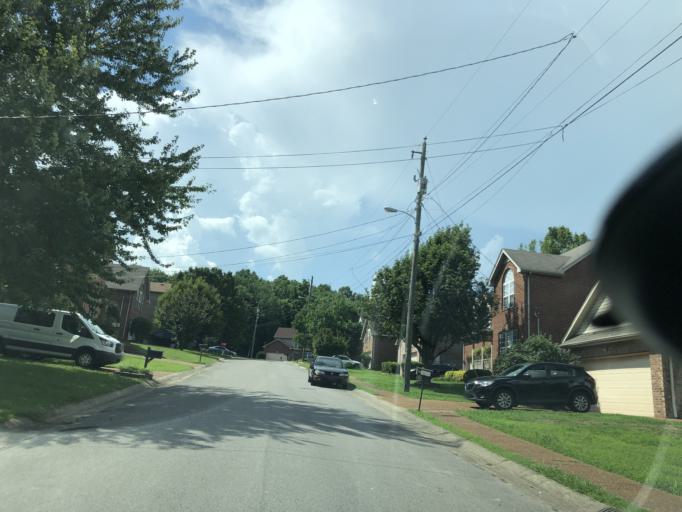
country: US
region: Tennessee
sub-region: Rutherford County
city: La Vergne
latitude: 36.0101
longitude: -86.6272
